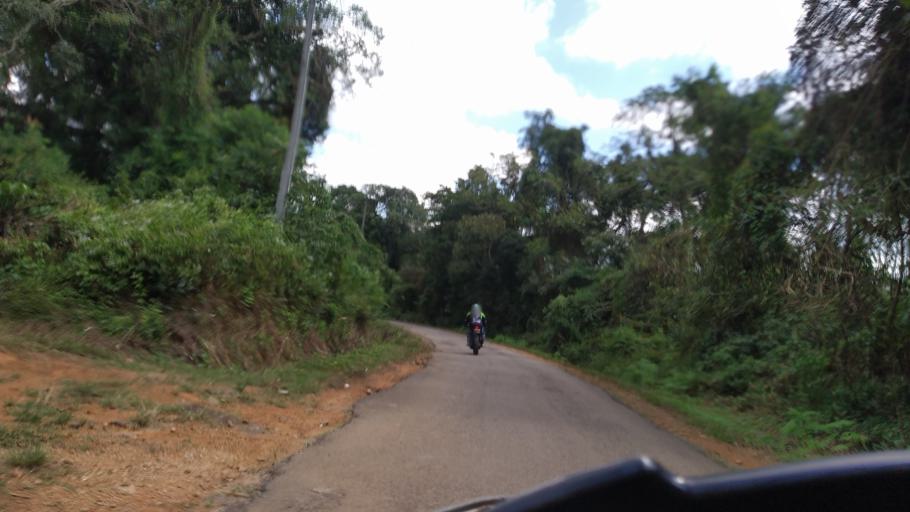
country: IN
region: Karnataka
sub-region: Kodagu
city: Ponnampet
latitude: 12.0241
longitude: 75.8900
